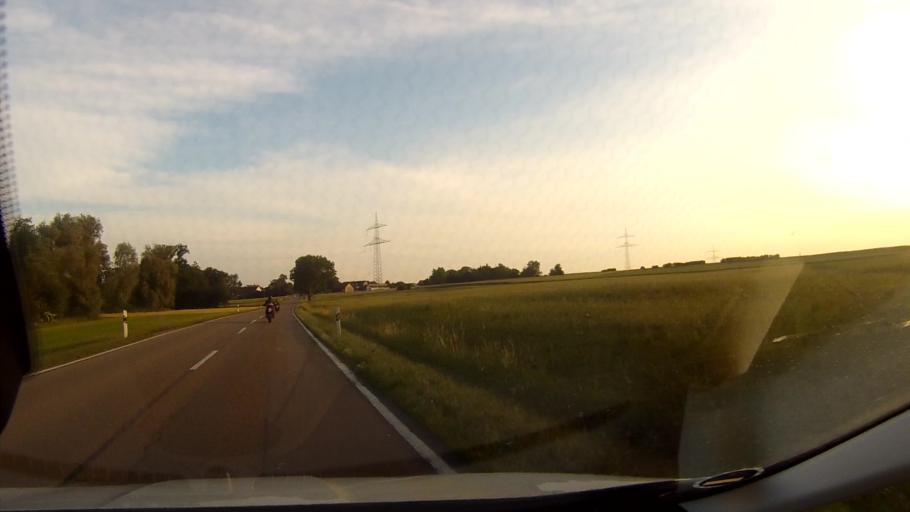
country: DE
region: Bavaria
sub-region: Swabia
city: Senden
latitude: 48.3118
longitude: 10.0185
